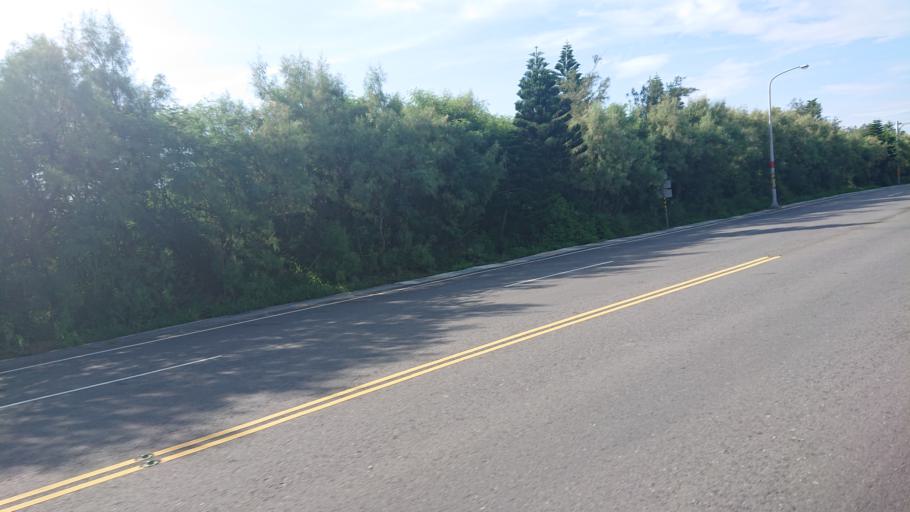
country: TW
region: Taiwan
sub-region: Penghu
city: Ma-kung
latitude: 23.5216
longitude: 119.5829
